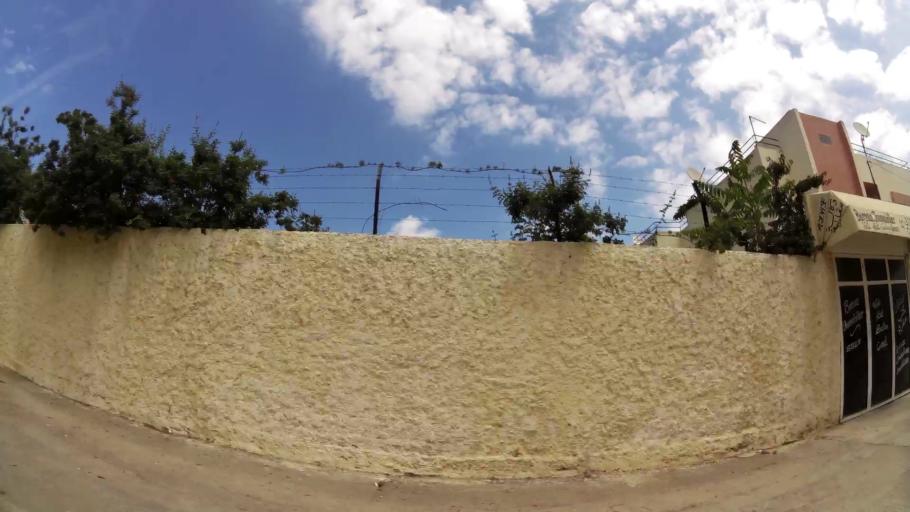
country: MA
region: Gharb-Chrarda-Beni Hssen
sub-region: Kenitra Province
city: Kenitra
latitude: 34.2625
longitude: -6.5954
